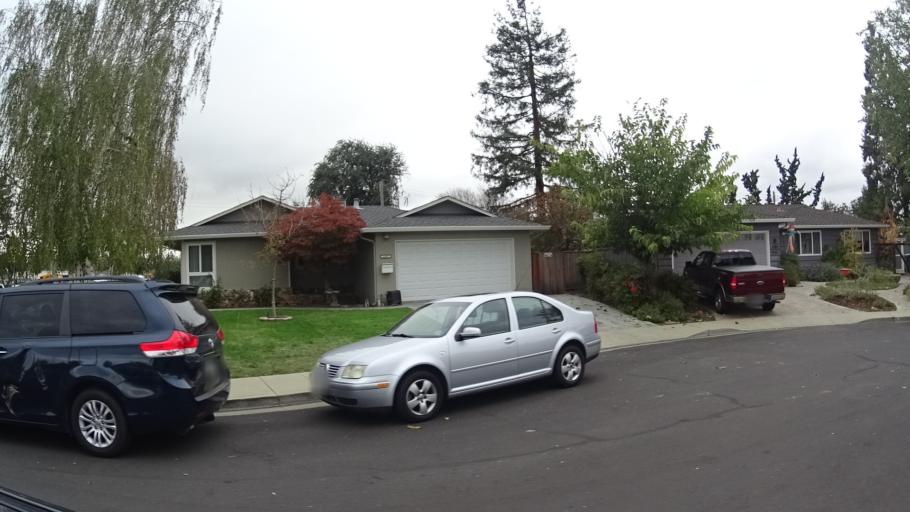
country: US
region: California
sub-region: Santa Clara County
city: Santa Clara
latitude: 37.3347
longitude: -121.9864
